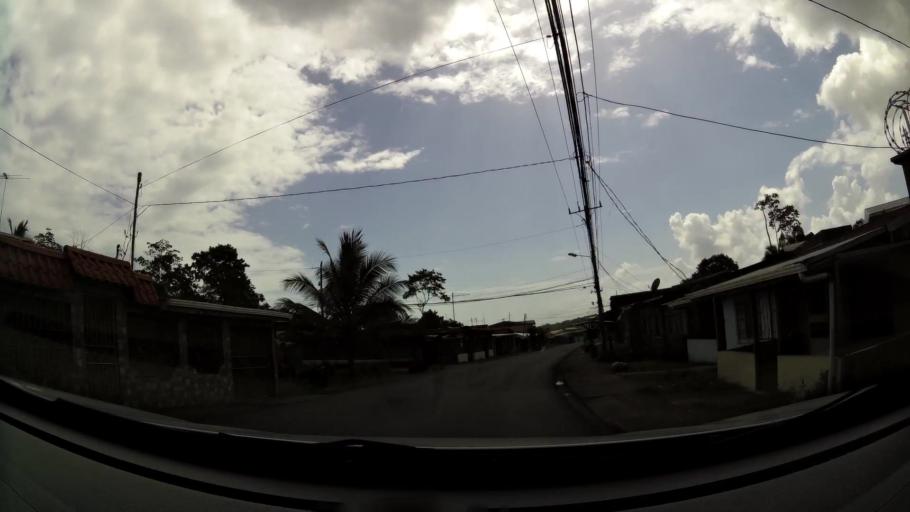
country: CR
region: Limon
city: Limon
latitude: 9.9878
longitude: -83.0485
